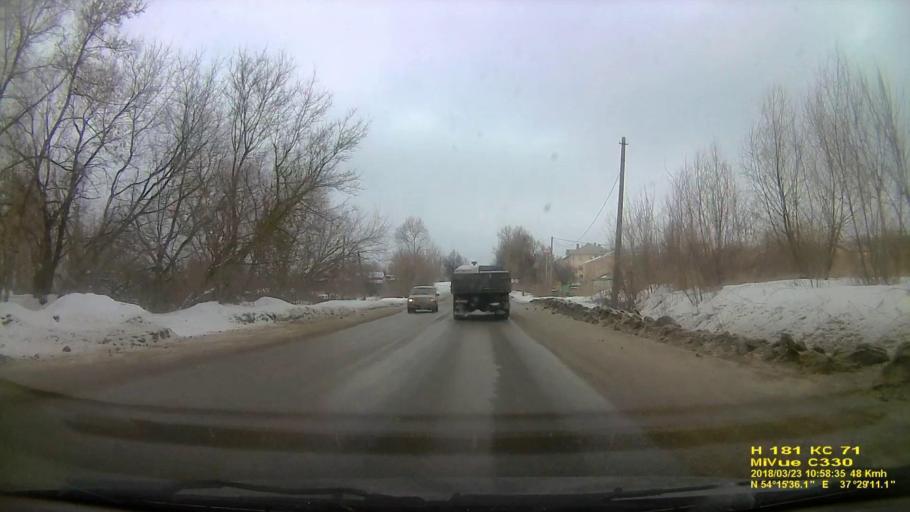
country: RU
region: Tula
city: Barsuki
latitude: 54.2601
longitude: 37.4864
